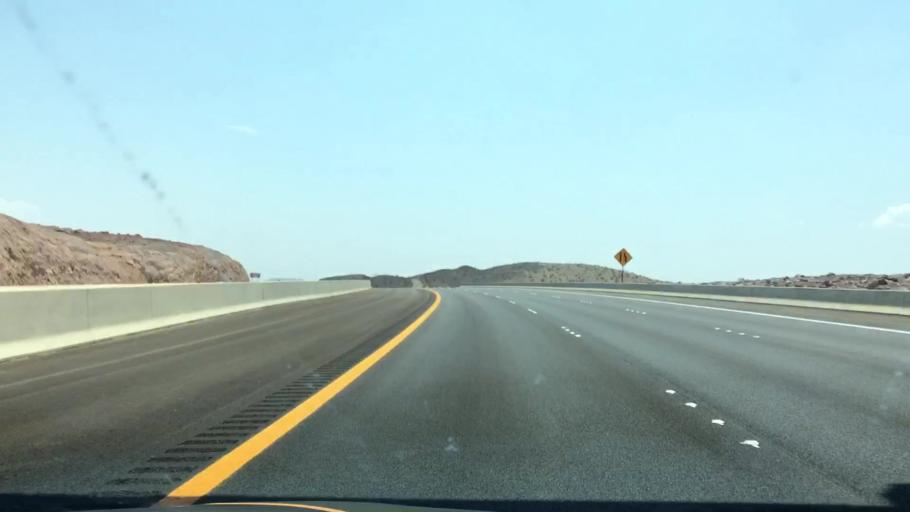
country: US
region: Nevada
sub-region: Clark County
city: Boulder City
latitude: 35.9920
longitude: -114.7996
